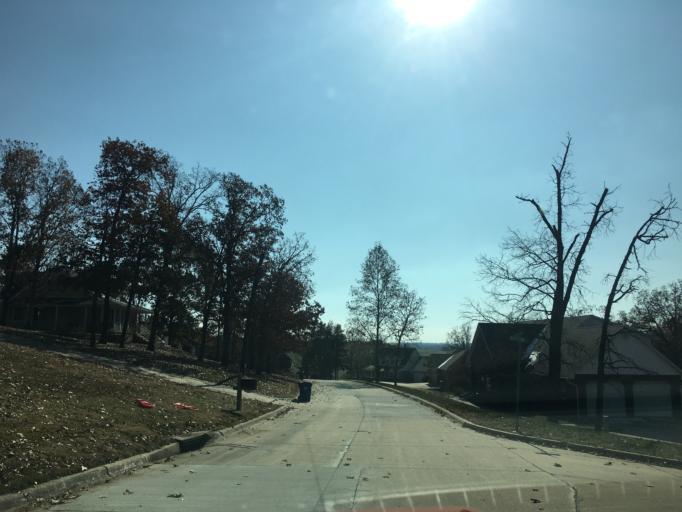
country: US
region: Missouri
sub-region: Cole County
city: Wardsville
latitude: 38.4820
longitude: -92.1794
